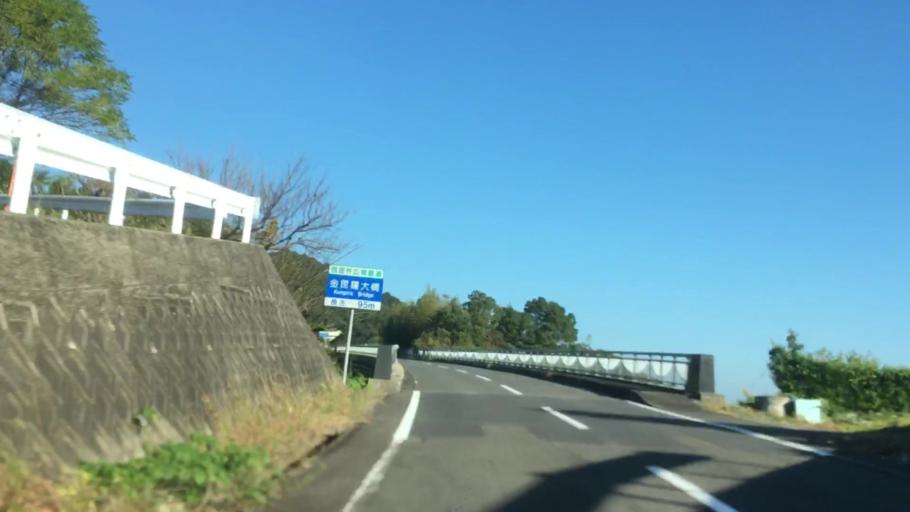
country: JP
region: Nagasaki
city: Sasebo
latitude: 32.9927
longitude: 129.7222
